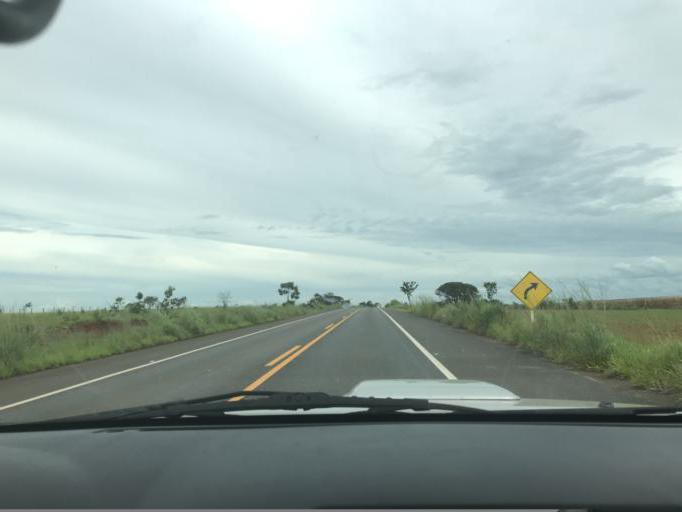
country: BR
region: Minas Gerais
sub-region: Araxa
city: Araxa
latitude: -19.3906
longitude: -46.8568
